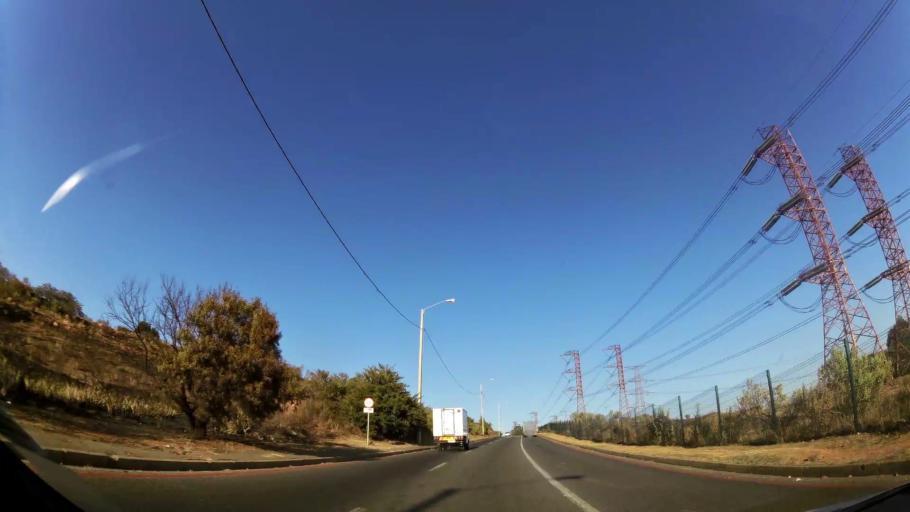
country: ZA
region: Gauteng
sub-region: Ekurhuleni Metropolitan Municipality
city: Germiston
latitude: -26.1769
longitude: 28.1594
